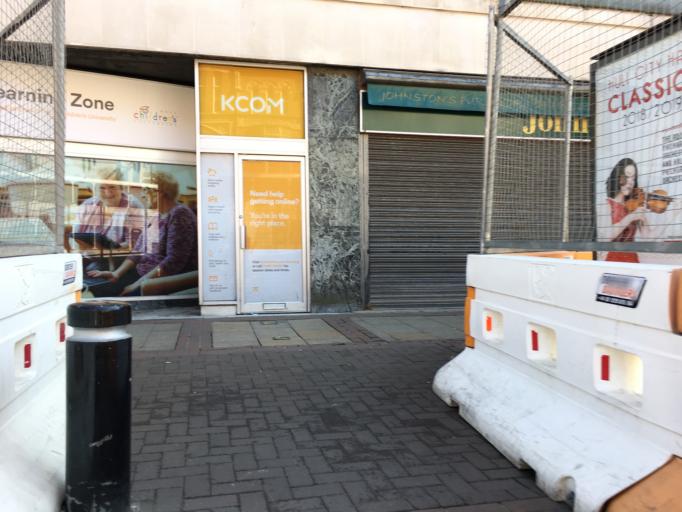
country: GB
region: England
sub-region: City of Kingston upon Hull
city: Hull
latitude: 53.7435
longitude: -0.3420
